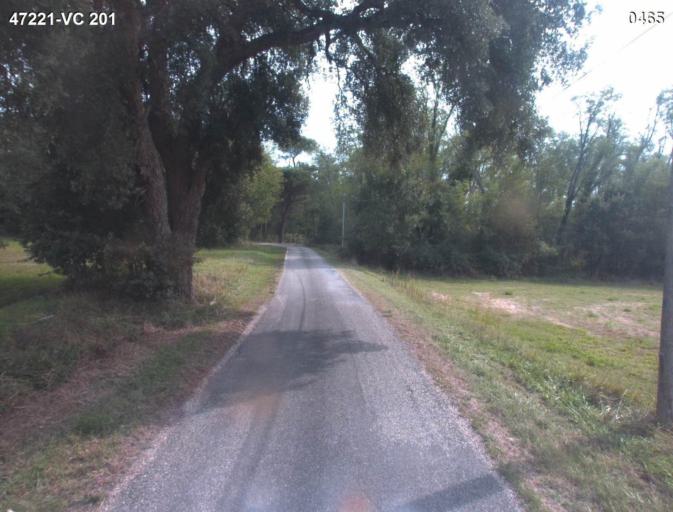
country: FR
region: Aquitaine
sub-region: Departement du Lot-et-Garonne
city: Mezin
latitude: 44.1162
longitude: 0.2275
